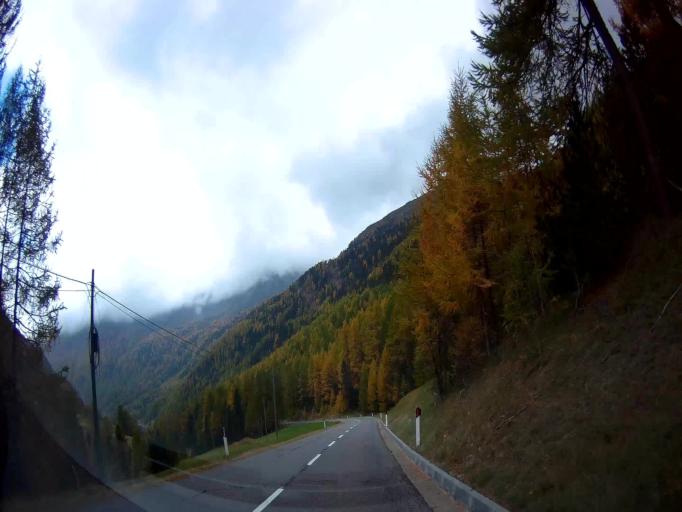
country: IT
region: Trentino-Alto Adige
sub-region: Bolzano
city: Silandro
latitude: 46.7419
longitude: 10.7900
